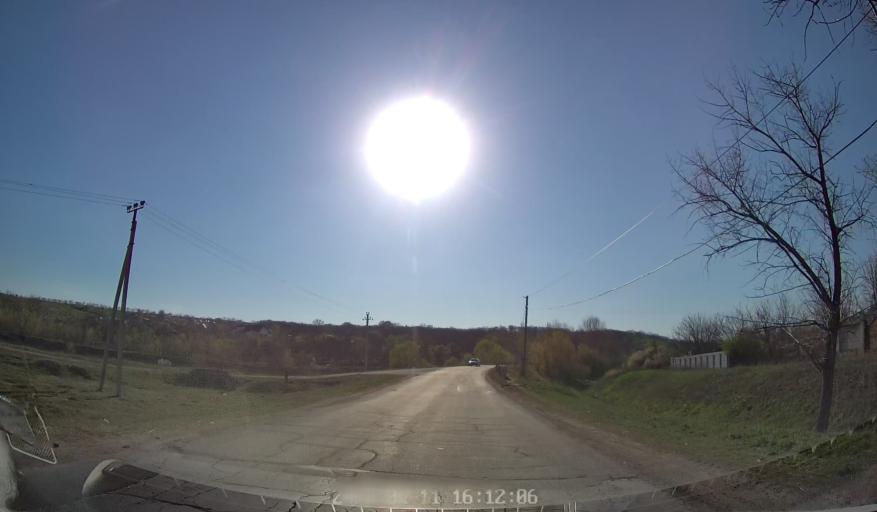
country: MD
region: Chisinau
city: Vadul lui Voda
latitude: 47.0694
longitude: 29.1252
